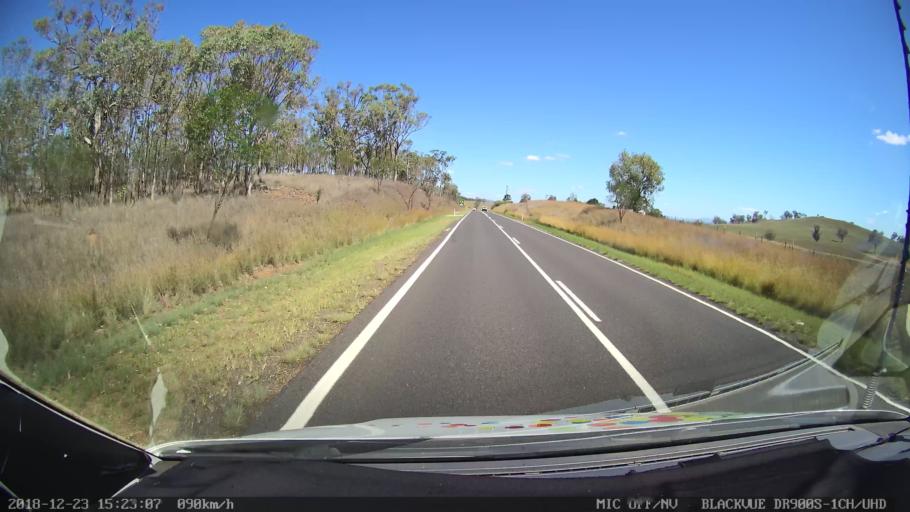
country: AU
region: New South Wales
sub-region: Tamworth Municipality
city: Manilla
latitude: -30.8764
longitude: 150.8111
